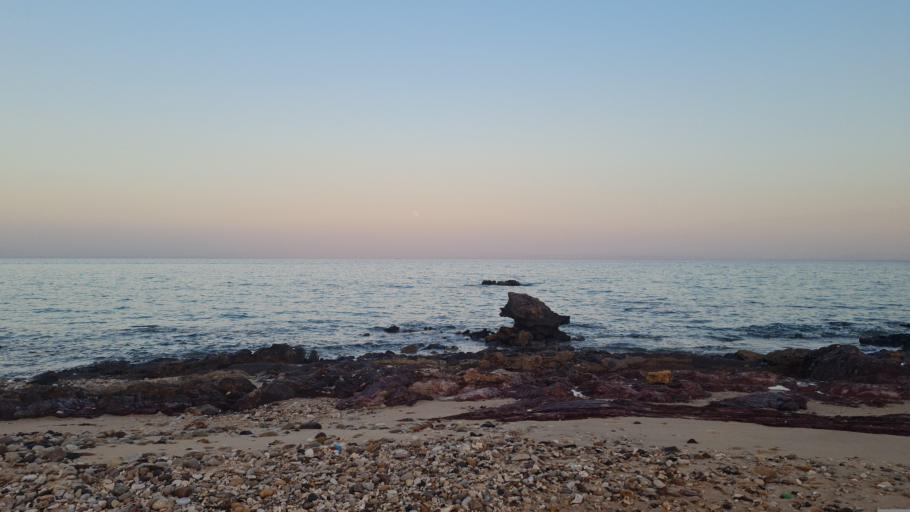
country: EG
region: As Suways
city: Ain Sukhna
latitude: 29.3256
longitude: 32.5982
